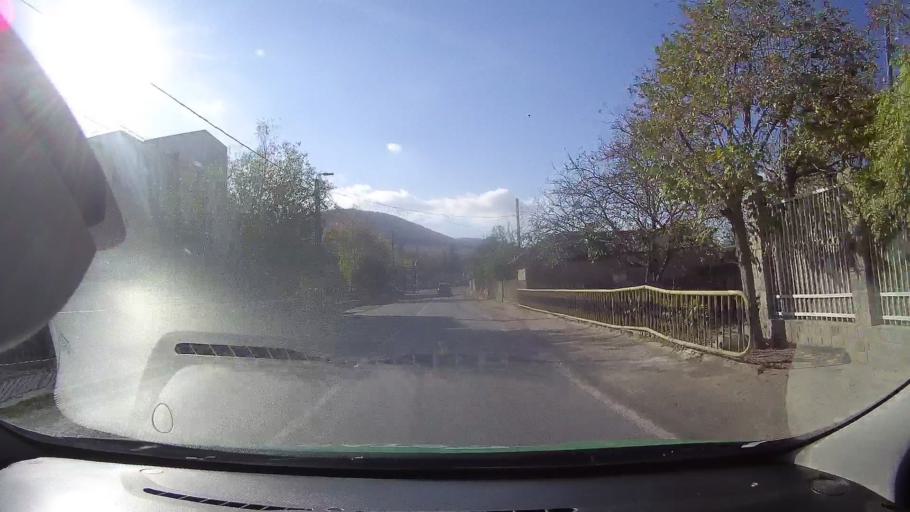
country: RO
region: Tulcea
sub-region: Oras Babadag
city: Babadag
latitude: 44.8922
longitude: 28.7172
